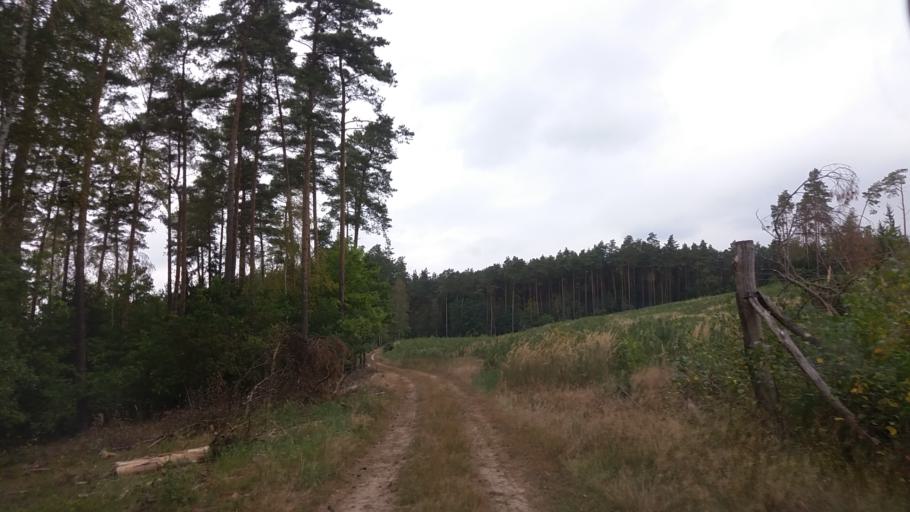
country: PL
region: West Pomeranian Voivodeship
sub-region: Powiat choszczenski
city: Bierzwnik
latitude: 52.9845
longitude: 15.6107
